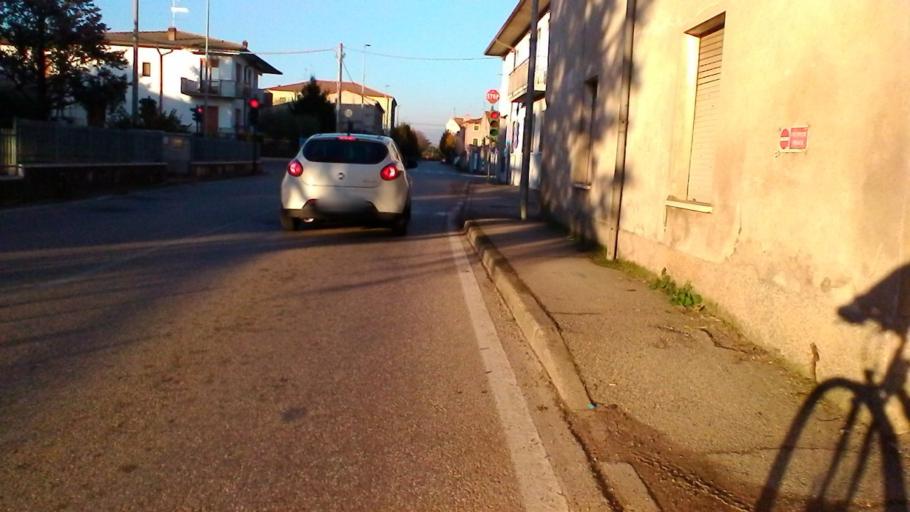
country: IT
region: Veneto
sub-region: Provincia di Verona
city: Alpo
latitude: 45.3708
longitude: 10.9123
